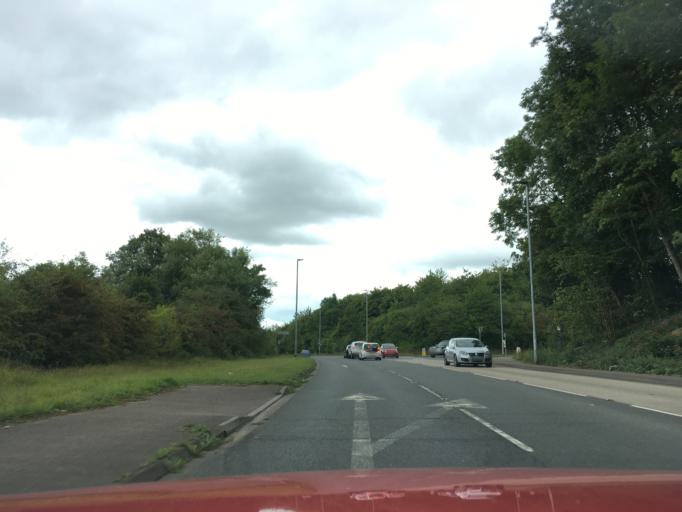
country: GB
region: England
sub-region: Devon
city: Exminster
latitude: 50.6875
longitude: -3.5015
